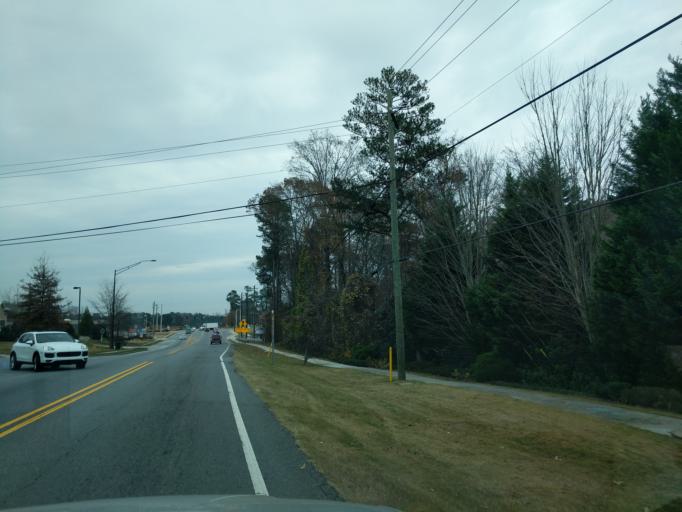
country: US
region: Georgia
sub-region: Gwinnett County
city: Duluth
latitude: 33.9784
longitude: -84.1028
